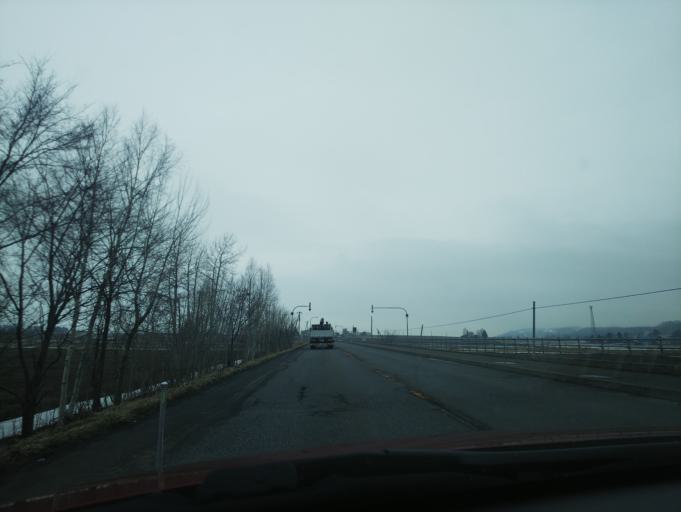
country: JP
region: Hokkaido
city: Nayoro
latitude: 44.0664
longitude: 142.3978
